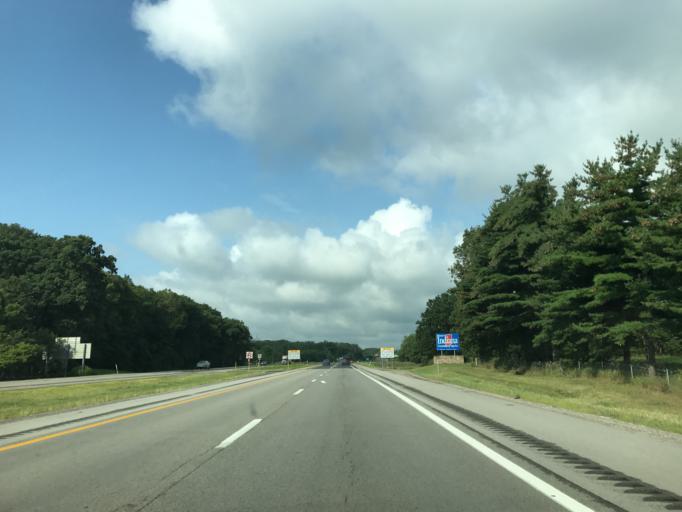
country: US
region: Indiana
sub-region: Steuben County
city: Hamilton
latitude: 41.6288
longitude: -84.8044
